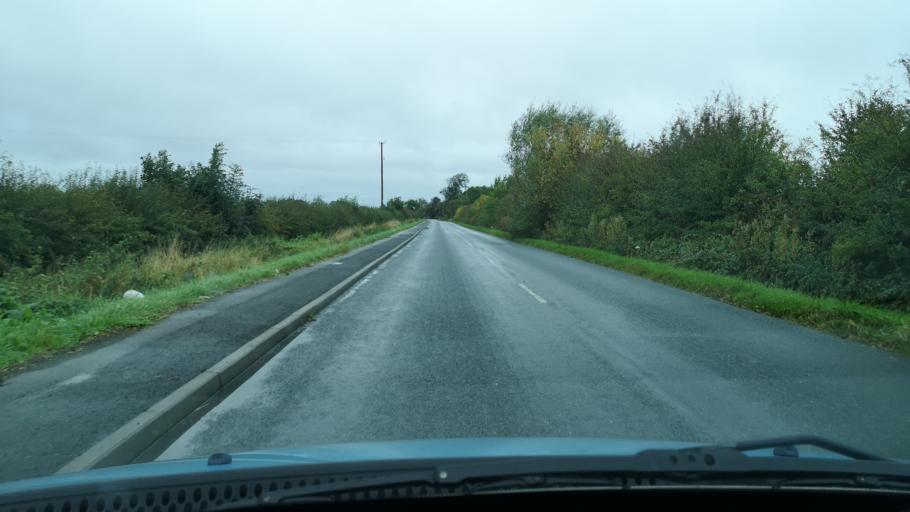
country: GB
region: England
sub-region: Doncaster
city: Stainforth
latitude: 53.6048
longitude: -1.0287
